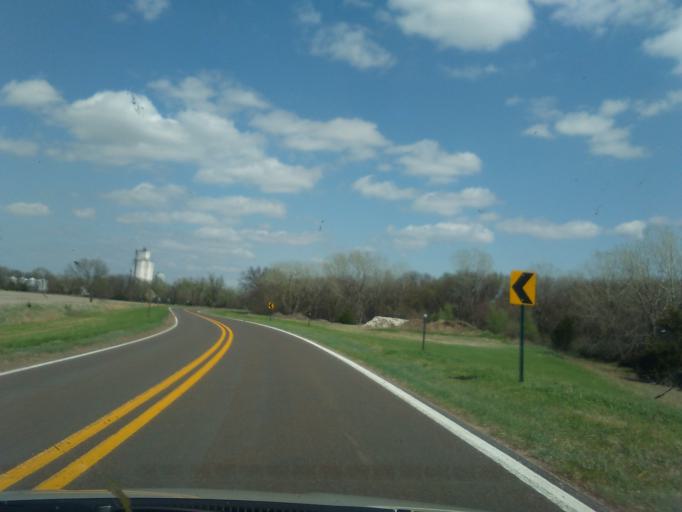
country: US
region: Nebraska
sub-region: Thayer County
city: Hebron
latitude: 40.2491
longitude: -97.5639
